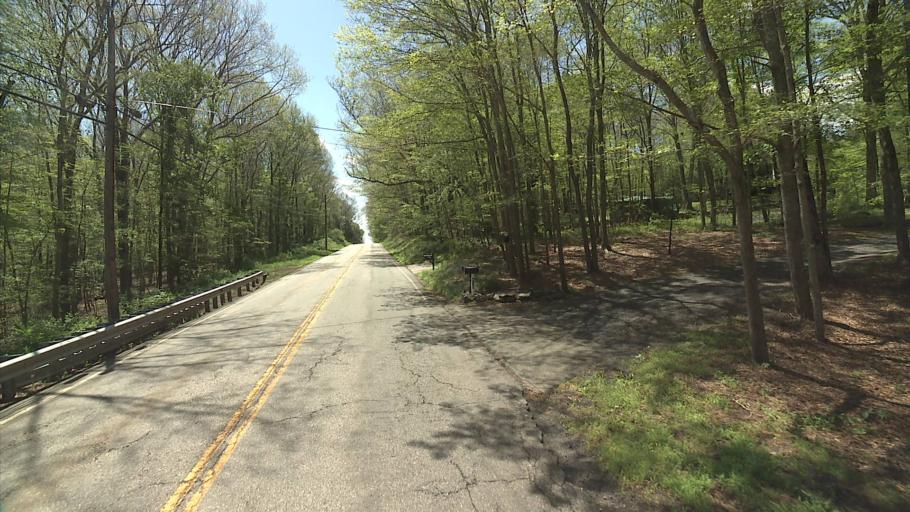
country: US
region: Connecticut
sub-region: Middlesex County
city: East Hampton
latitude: 41.5329
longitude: -72.4952
